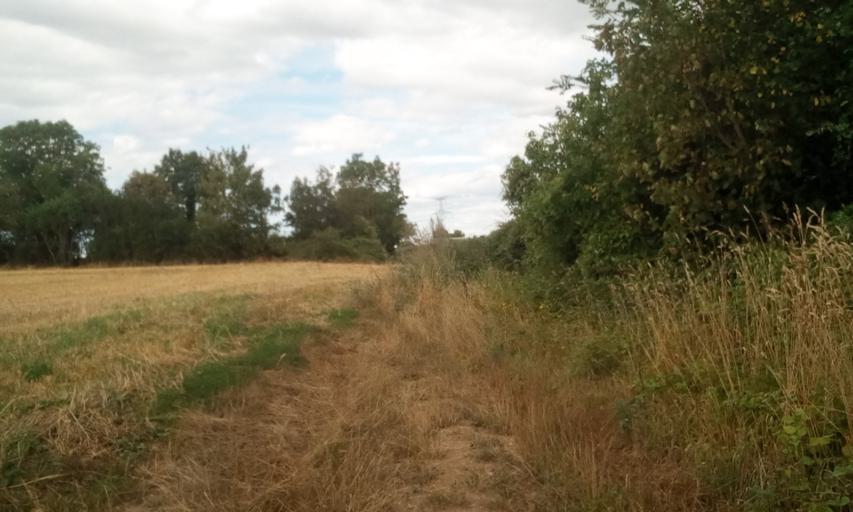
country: FR
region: Lower Normandy
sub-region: Departement du Calvados
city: Bellengreville
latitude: 49.1292
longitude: -0.1971
